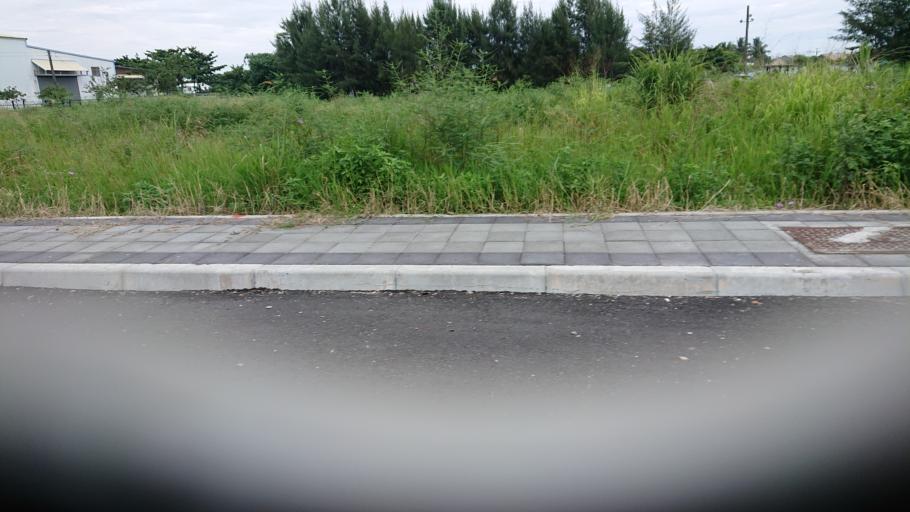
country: TW
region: Taiwan
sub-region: Hualien
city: Hualian
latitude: 23.9609
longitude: 121.6041
